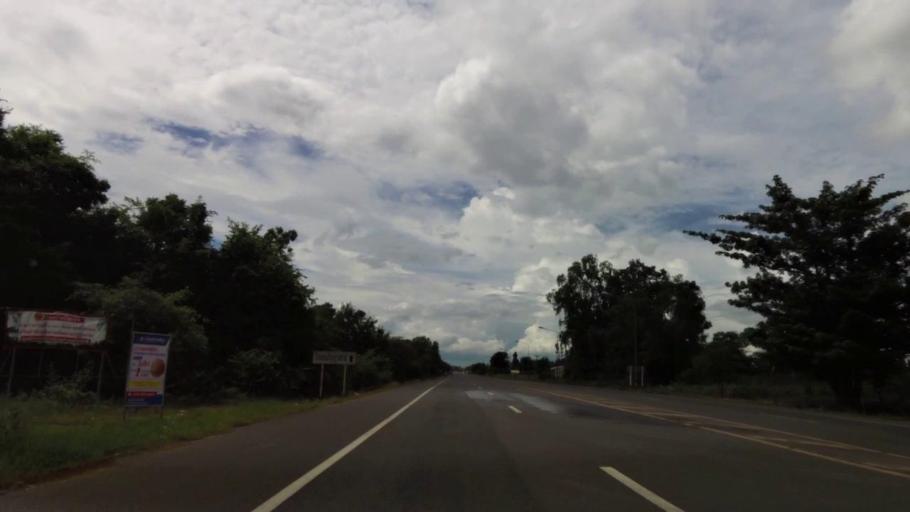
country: TH
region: Nakhon Sawan
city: Phai Sali
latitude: 15.5993
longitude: 100.6675
